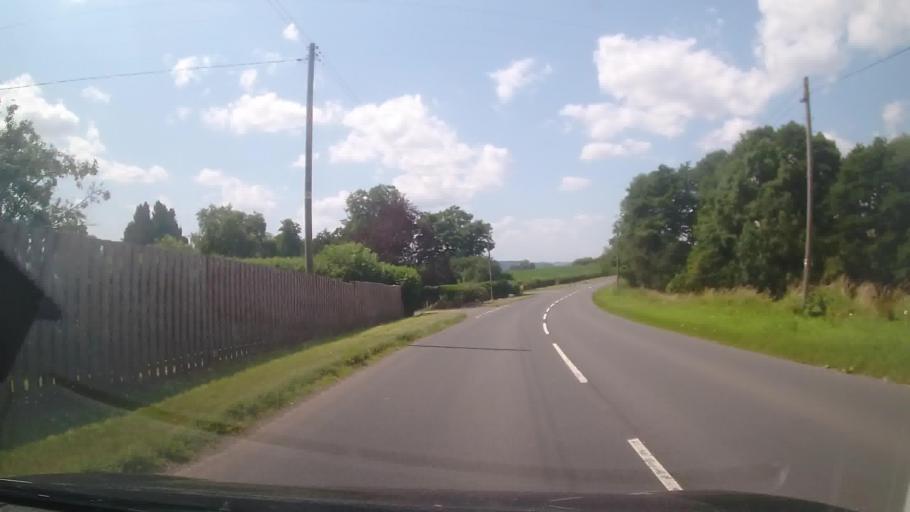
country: GB
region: England
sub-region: Herefordshire
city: Ocle Pychard
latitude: 52.1441
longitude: -2.6235
